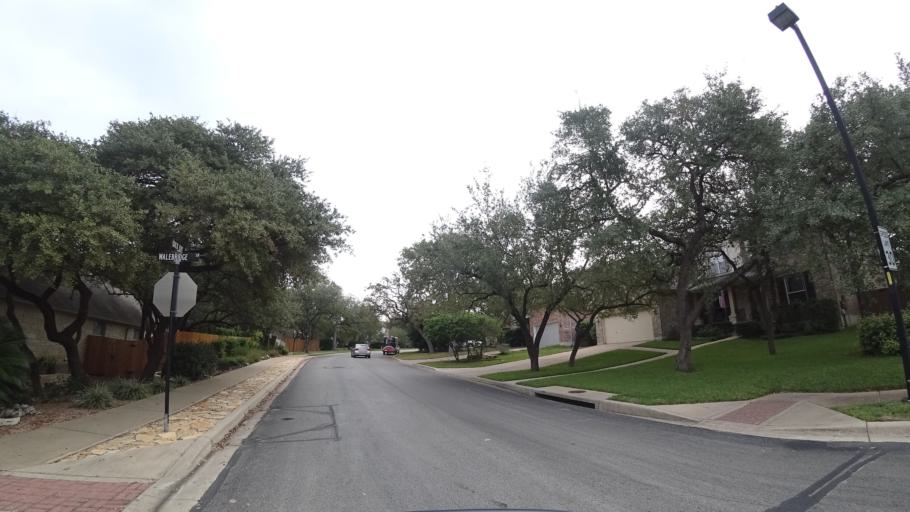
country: US
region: Texas
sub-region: Travis County
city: Shady Hollow
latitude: 30.1898
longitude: -97.8981
